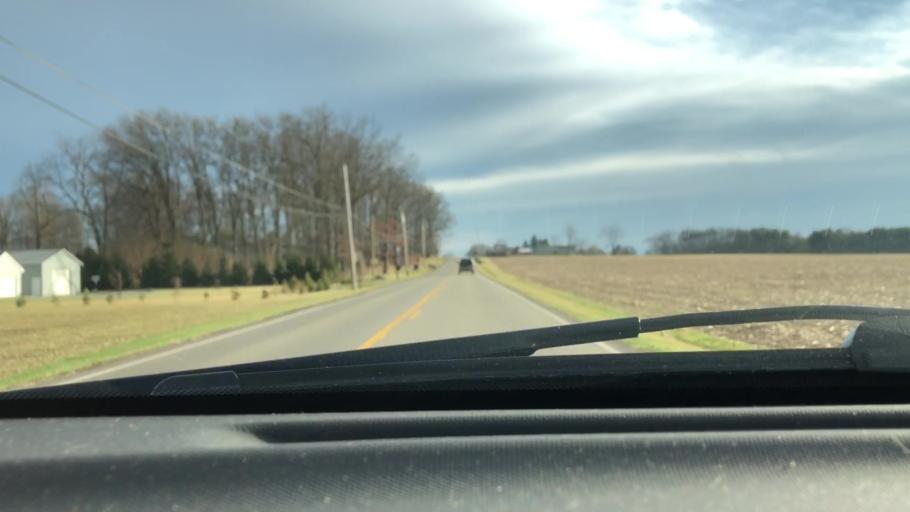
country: US
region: Ohio
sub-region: Wayne County
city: Dalton
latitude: 40.7914
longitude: -81.7454
